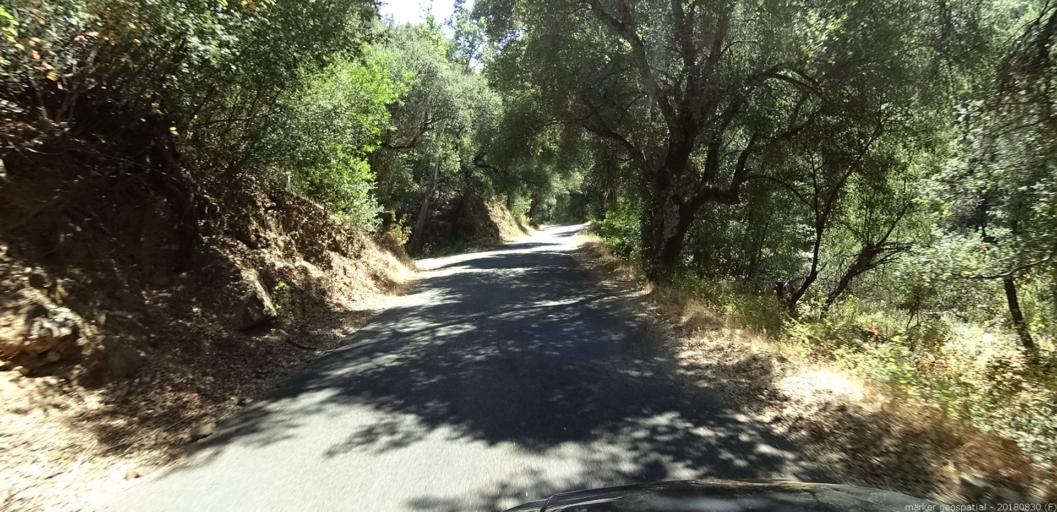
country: US
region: California
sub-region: Monterey County
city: King City
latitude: 36.0138
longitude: -121.4108
